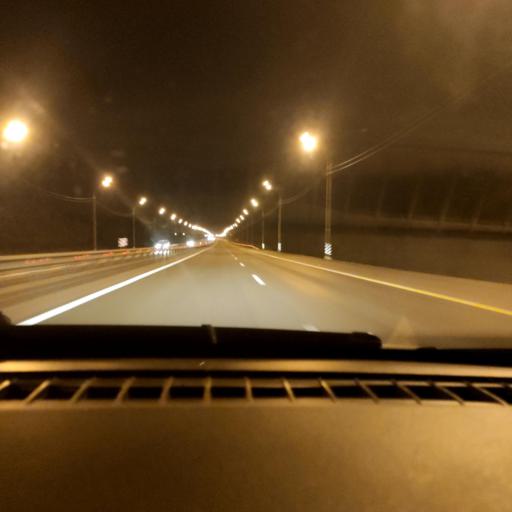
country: RU
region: Lipetsk
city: Khlevnoye
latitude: 52.2011
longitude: 39.1649
